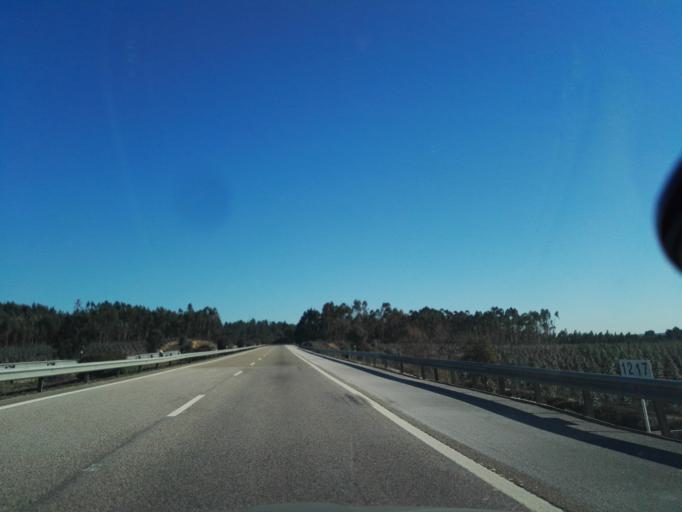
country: PT
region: Santarem
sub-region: Constancia
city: Constancia
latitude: 39.4851
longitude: -8.3766
